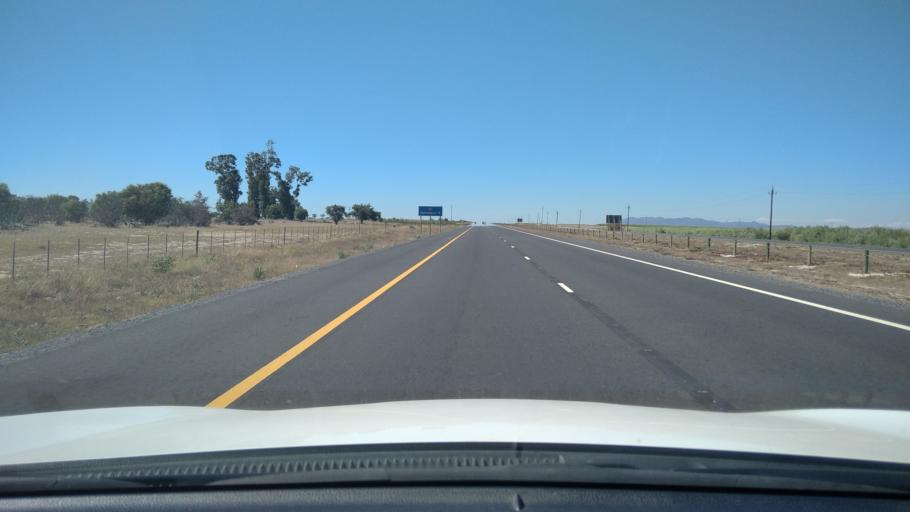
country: ZA
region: Western Cape
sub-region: West Coast District Municipality
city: Malmesbury
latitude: -33.5593
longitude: 18.6268
